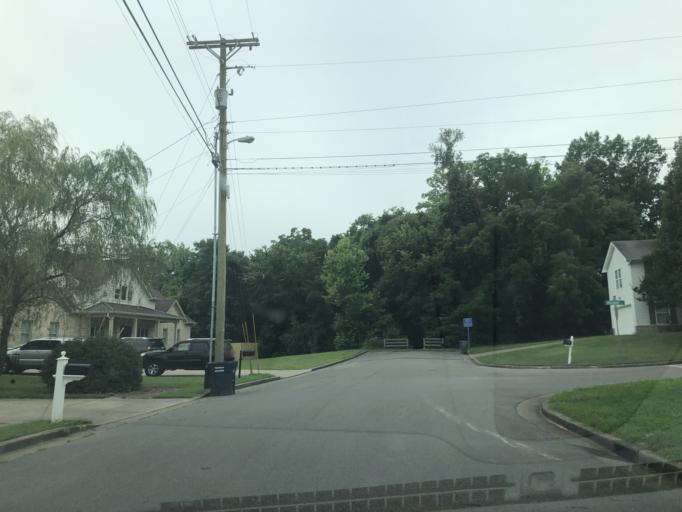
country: US
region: Tennessee
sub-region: Williamson County
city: Nolensville
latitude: 36.0179
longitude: -86.6891
